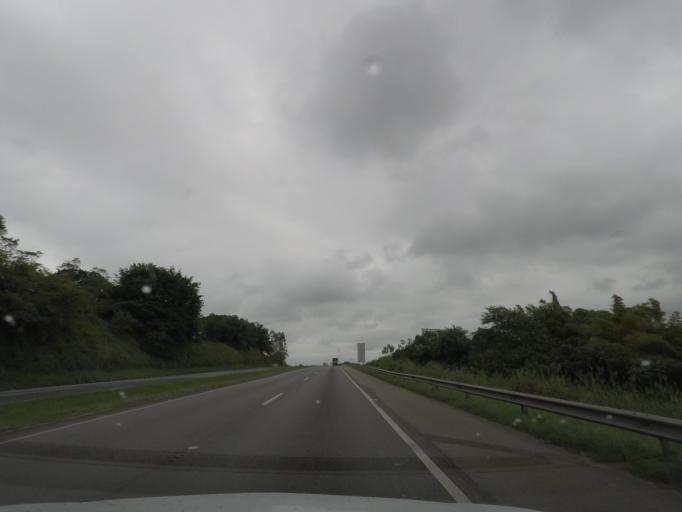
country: BR
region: Sao Paulo
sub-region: Registro
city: Registro
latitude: -24.4512
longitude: -47.8092
